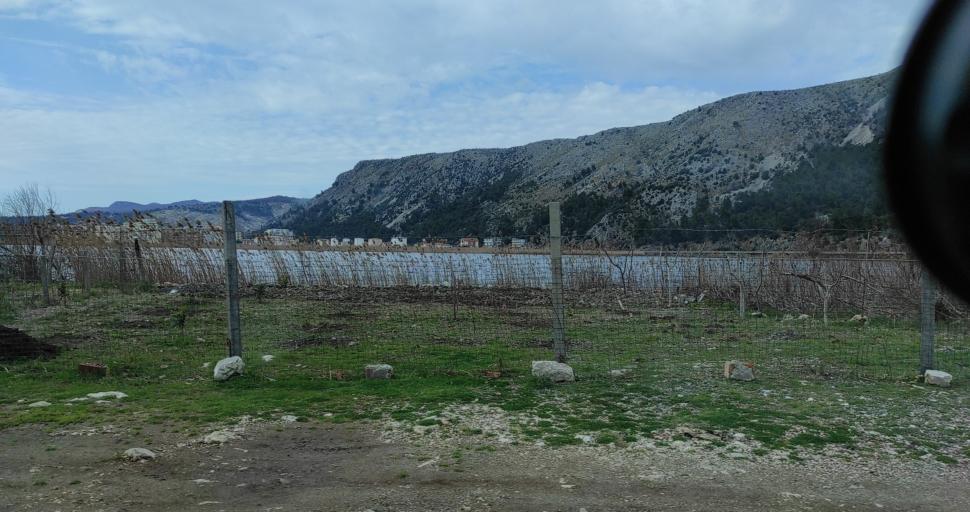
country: AL
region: Lezhe
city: Shengjin
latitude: 41.7994
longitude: 19.6133
